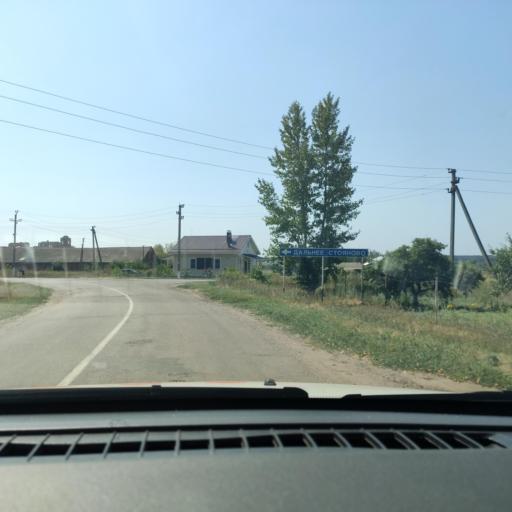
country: RU
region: Voronezj
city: Ostrogozhsk
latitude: 50.7071
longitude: 39.3333
